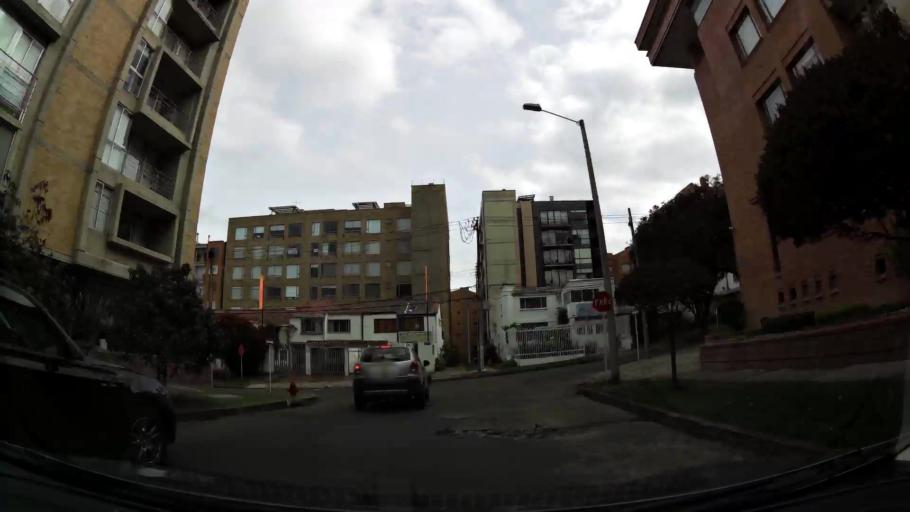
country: CO
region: Bogota D.C.
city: Barrio San Luis
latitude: 4.7074
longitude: -74.0312
